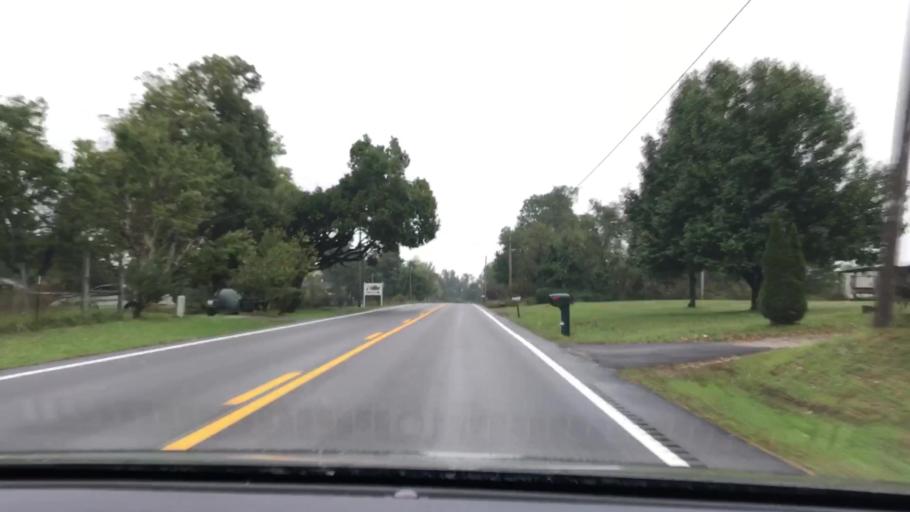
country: US
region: Tennessee
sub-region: Fentress County
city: Grimsley
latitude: 36.1746
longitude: -85.0544
